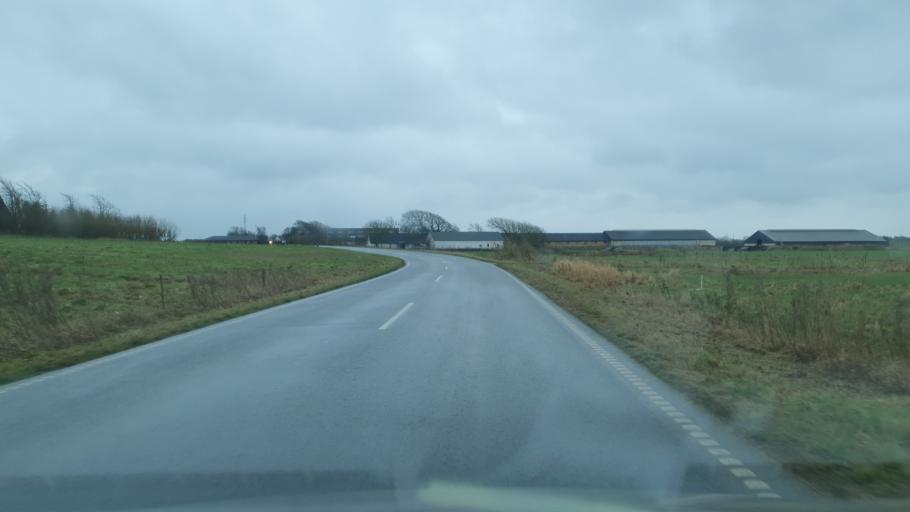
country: DK
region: North Denmark
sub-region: Jammerbugt Kommune
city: Fjerritslev
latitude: 57.1134
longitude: 9.1282
